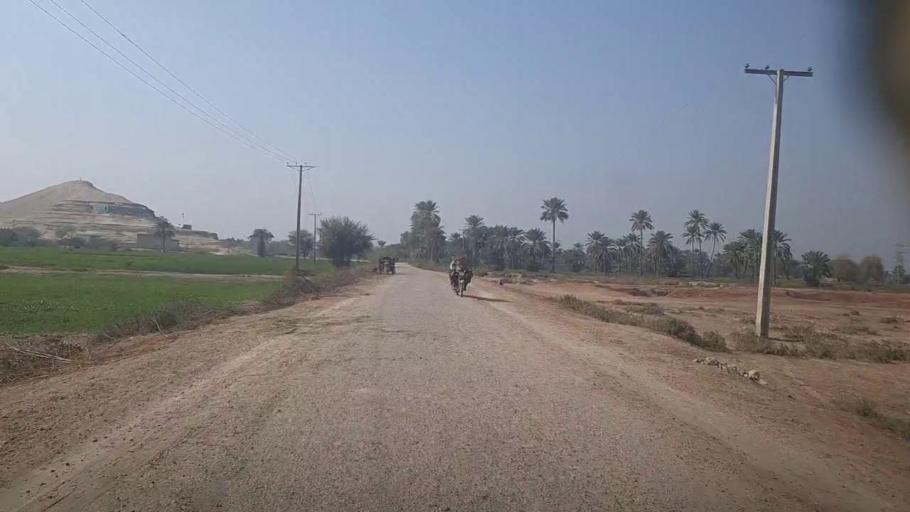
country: PK
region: Sindh
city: Kot Diji
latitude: 27.3487
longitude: 68.7210
